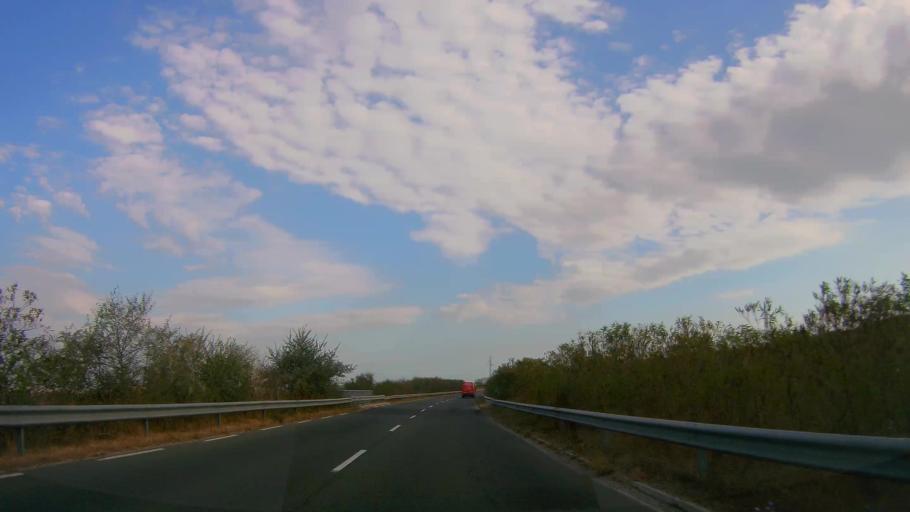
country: BG
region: Burgas
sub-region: Obshtina Sozopol
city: Sozopol
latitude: 42.3955
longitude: 27.6753
